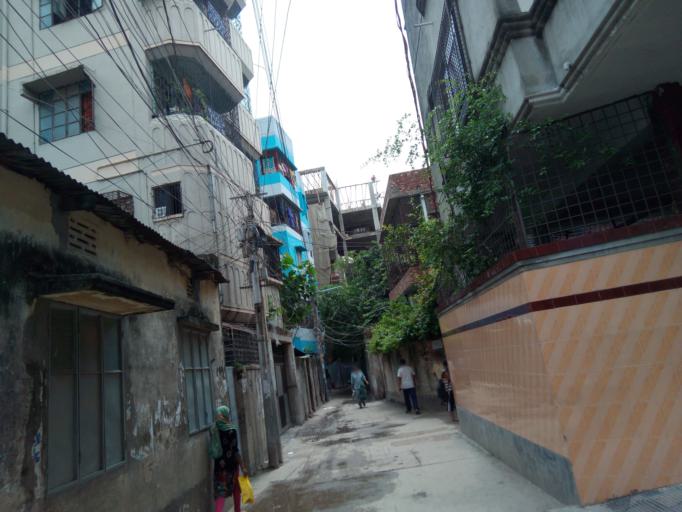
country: BD
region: Dhaka
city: Azimpur
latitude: 23.7477
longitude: 90.3640
